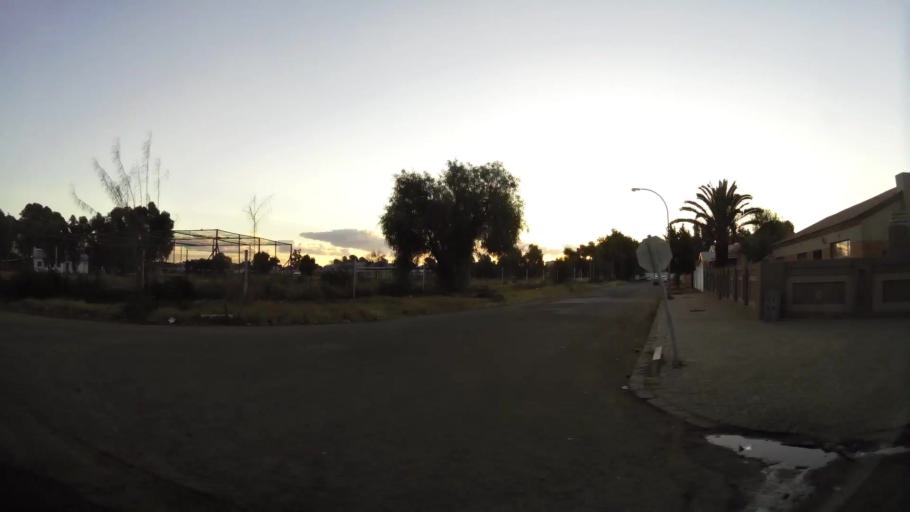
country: ZA
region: Northern Cape
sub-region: Frances Baard District Municipality
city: Kimberley
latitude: -28.7296
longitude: 24.7686
